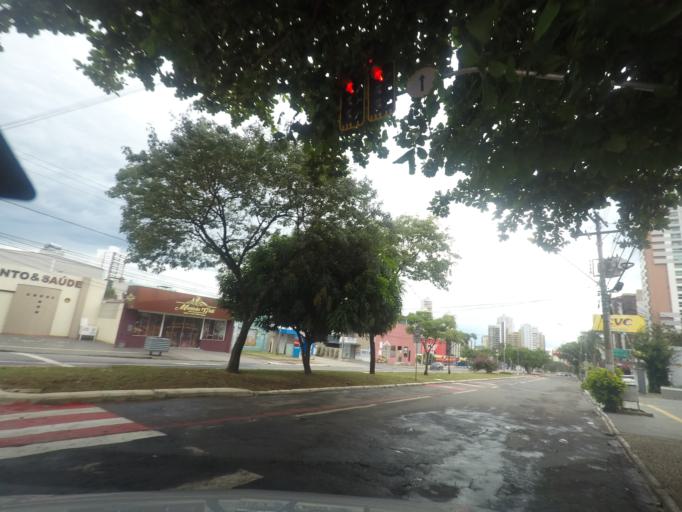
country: BR
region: Goias
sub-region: Goiania
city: Goiania
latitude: -16.6939
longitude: -49.2696
